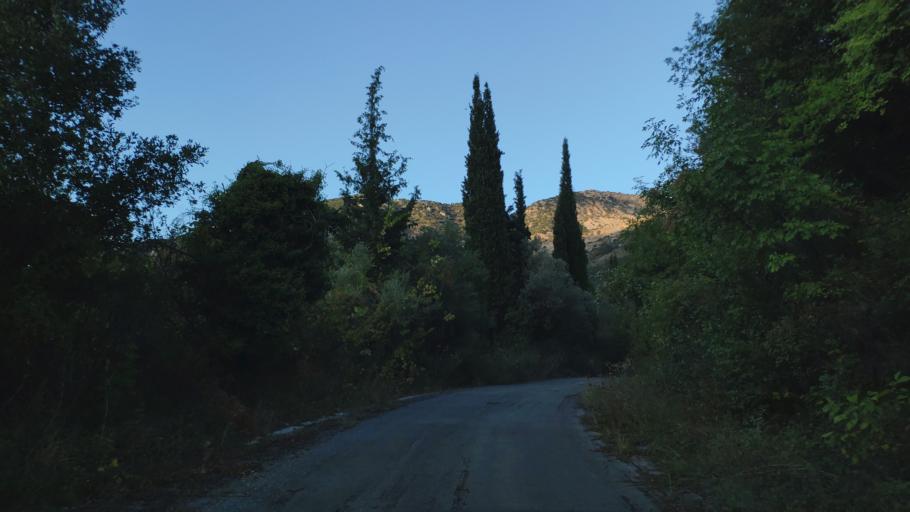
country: GR
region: Peloponnese
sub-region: Nomos Arkadias
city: Dimitsana
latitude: 37.5722
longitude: 22.0467
